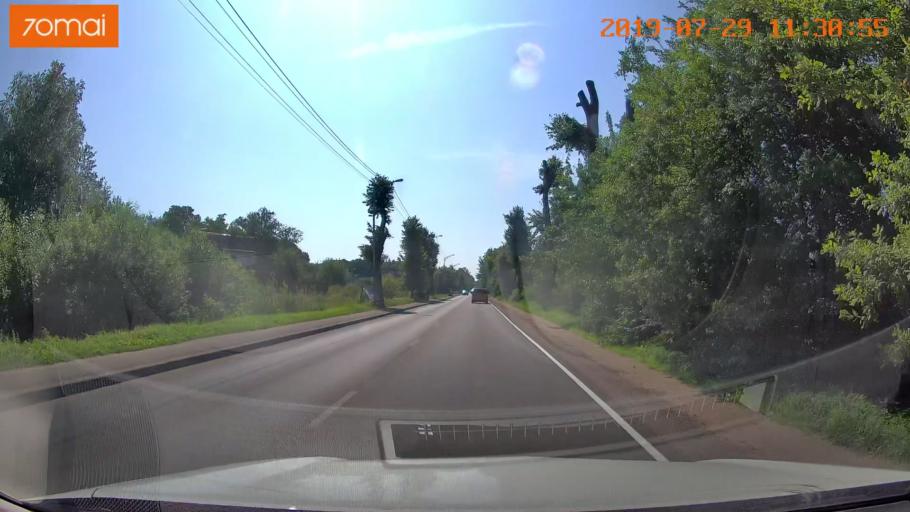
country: RU
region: Kaliningrad
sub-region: Gorod Kaliningrad
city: Kaliningrad
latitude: 54.6788
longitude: 20.5380
